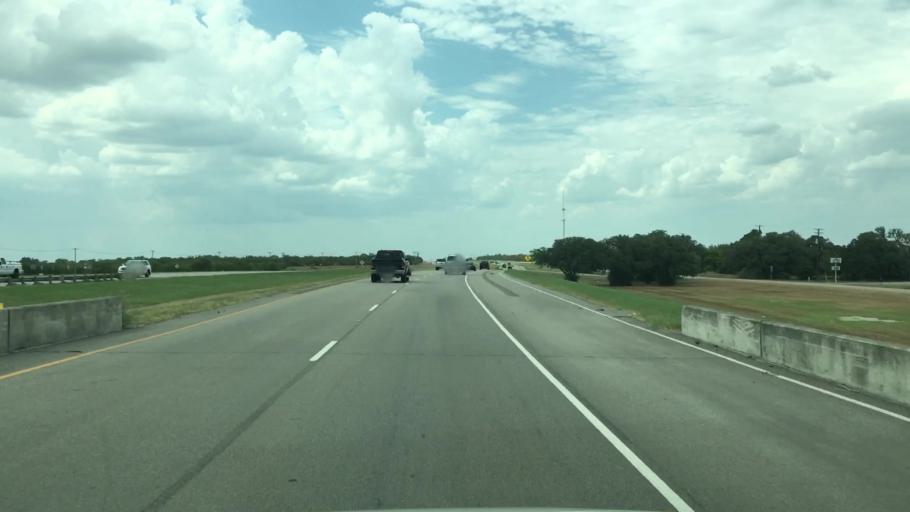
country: US
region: Texas
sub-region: Live Oak County
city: Three Rivers
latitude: 28.4895
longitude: -98.1432
